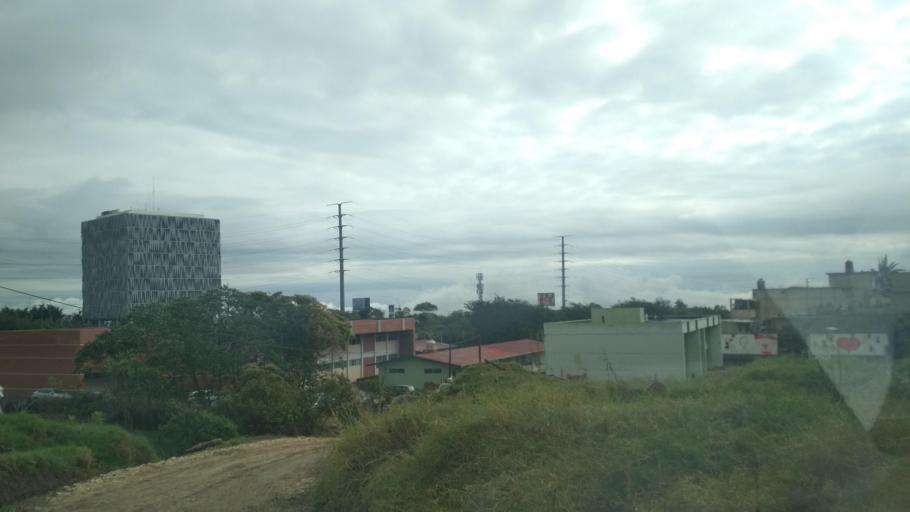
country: MX
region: Veracruz
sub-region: Xalapa
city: Colonia Santa Barbara
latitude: 19.5071
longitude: -96.8736
